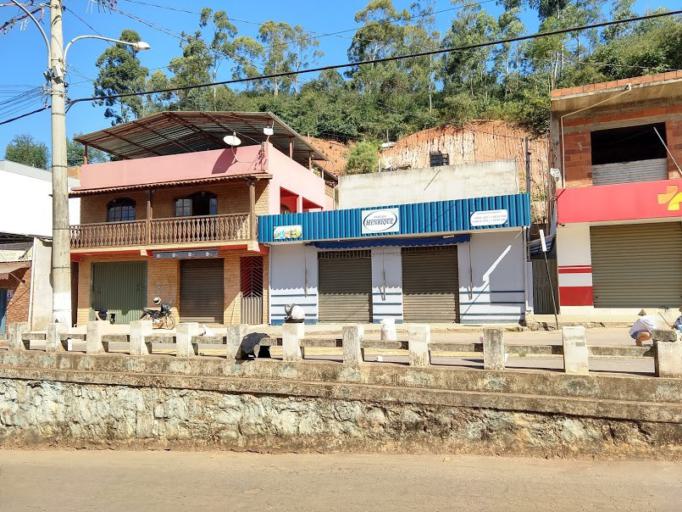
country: BR
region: Minas Gerais
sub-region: Vicosa
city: Vicosa
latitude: -20.6873
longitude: -42.6183
